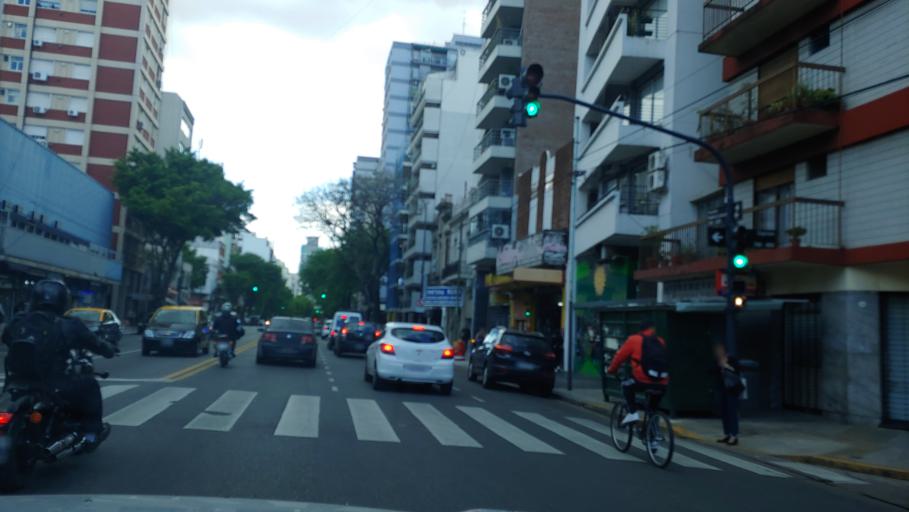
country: AR
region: Buenos Aires F.D.
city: Colegiales
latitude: -34.5760
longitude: -58.4484
